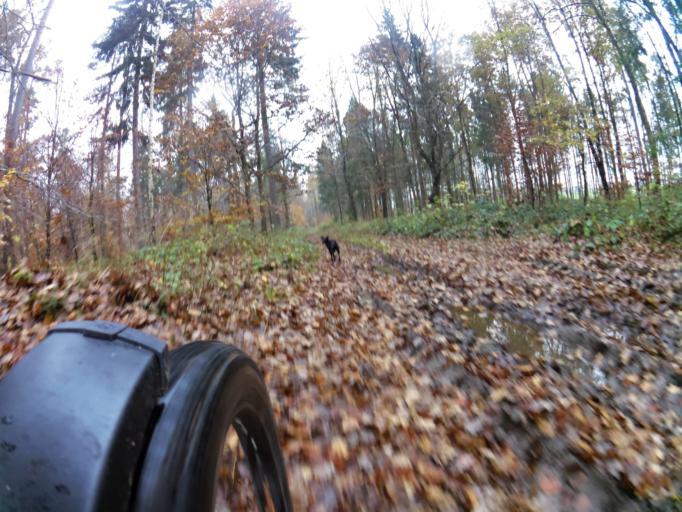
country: PL
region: Pomeranian Voivodeship
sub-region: Powiat pucki
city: Krokowa
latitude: 54.7363
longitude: 18.1303
